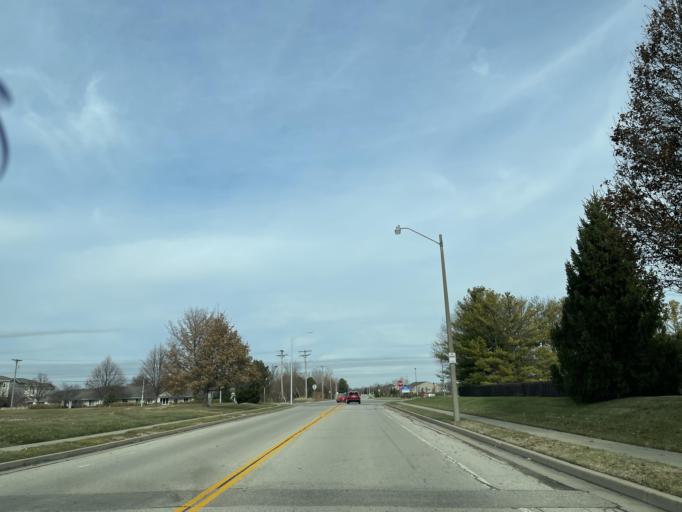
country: US
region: Illinois
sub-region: Sangamon County
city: Jerome
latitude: 39.7700
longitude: -89.7298
